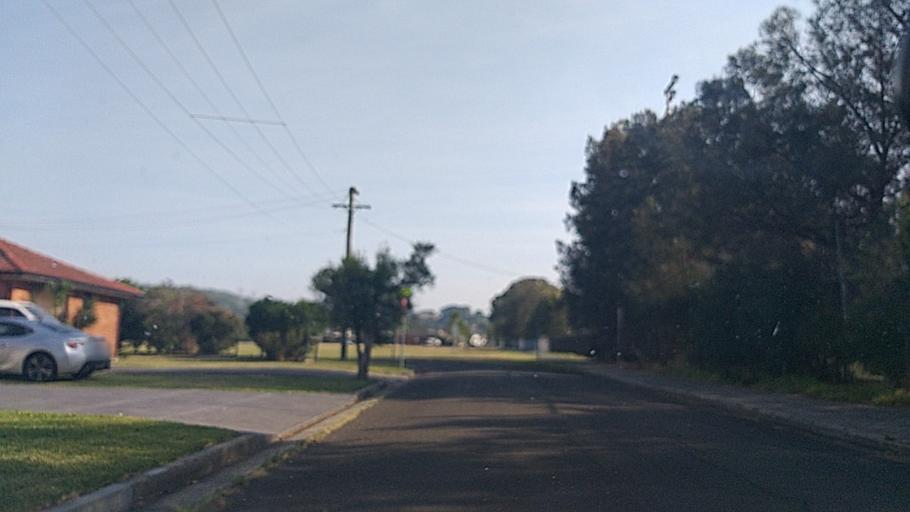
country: AU
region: New South Wales
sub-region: Wollongong
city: Berkeley
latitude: -34.4818
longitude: 150.8521
